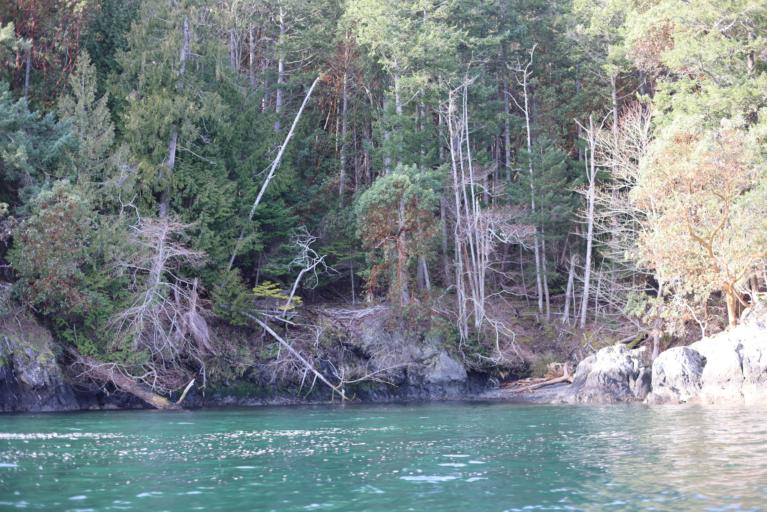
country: CA
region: British Columbia
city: Duncan
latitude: 48.7510
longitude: -123.5702
